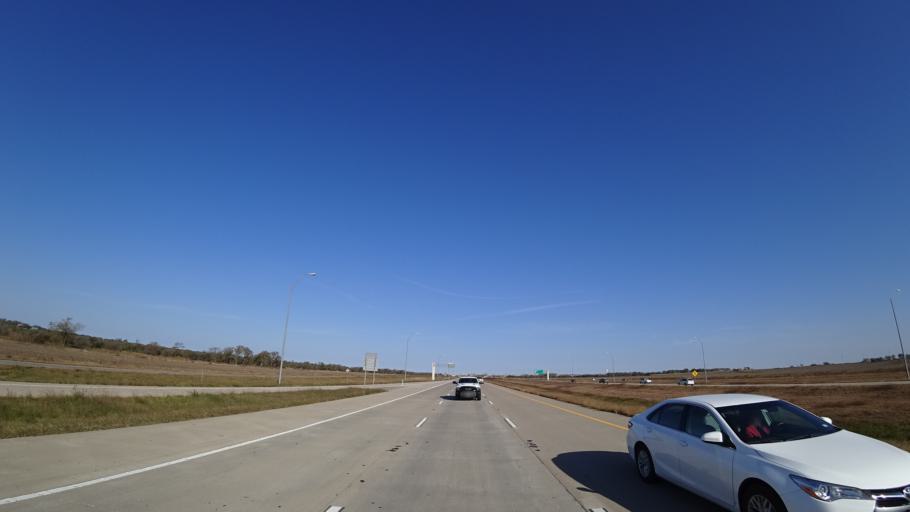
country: US
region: Texas
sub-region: Travis County
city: Pflugerville
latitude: 30.4350
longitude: -97.5912
